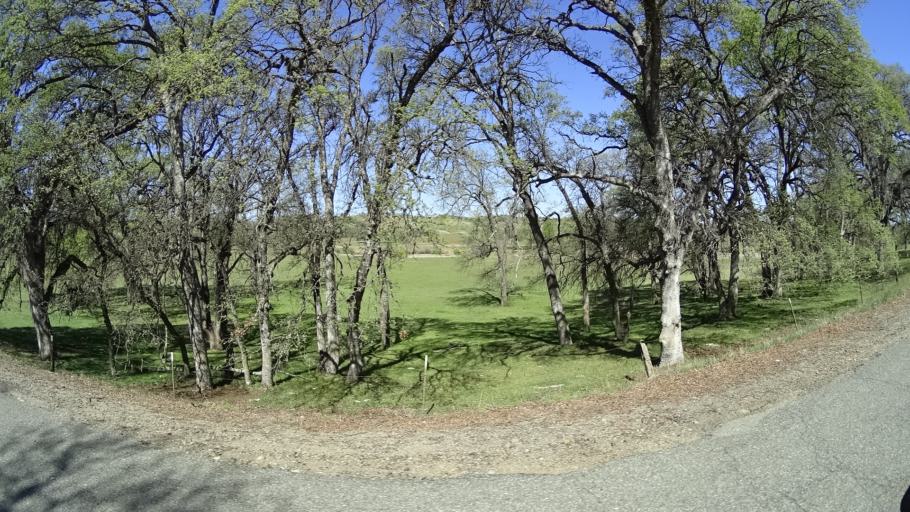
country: US
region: California
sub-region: Tehama County
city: Rancho Tehama Reserve
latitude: 39.7928
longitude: -122.4473
